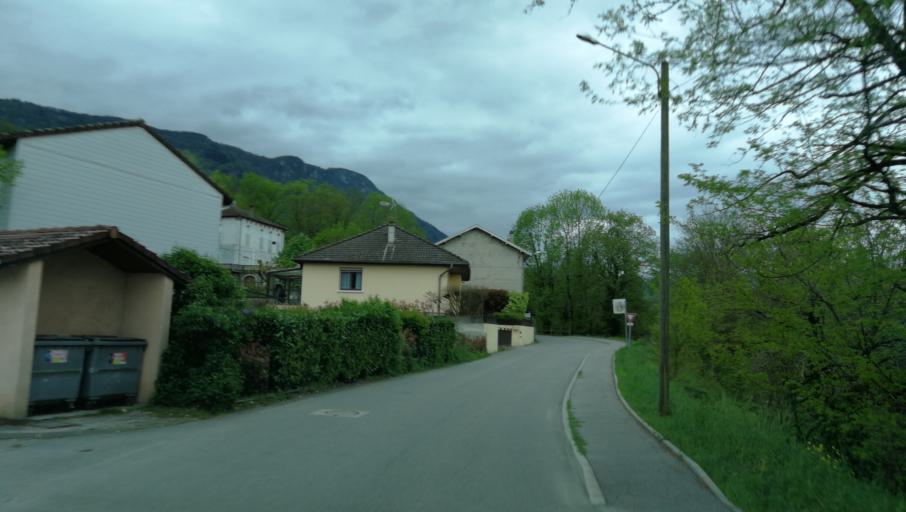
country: FR
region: Rhone-Alpes
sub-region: Departement de la Drome
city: Saint-Jean-en-Royans
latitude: 45.0135
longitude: 5.2886
